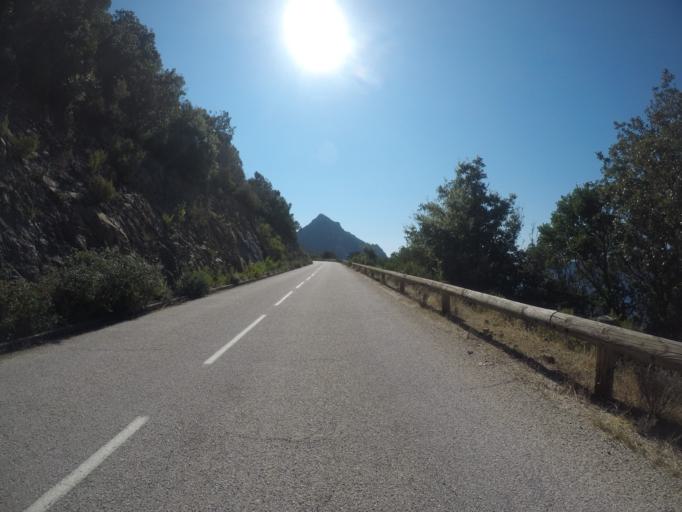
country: FR
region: Corsica
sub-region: Departement de la Corse-du-Sud
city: Cargese
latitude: 42.3315
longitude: 8.6373
